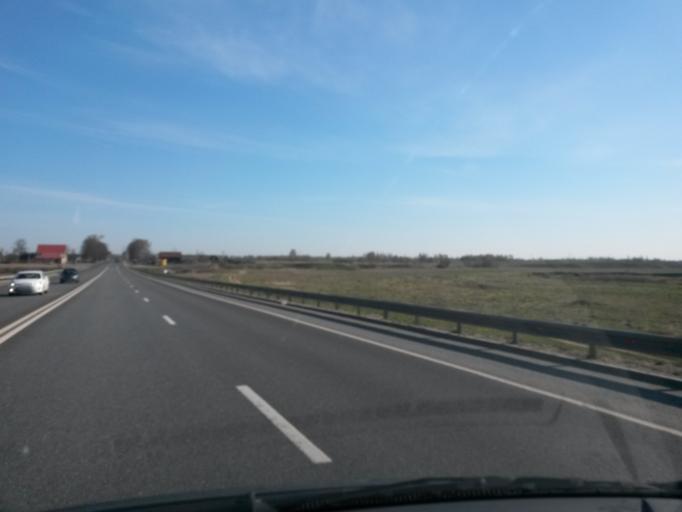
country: RU
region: Jaroslavl
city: Porech'ye-Rybnoye
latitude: 57.0887
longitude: 39.3124
